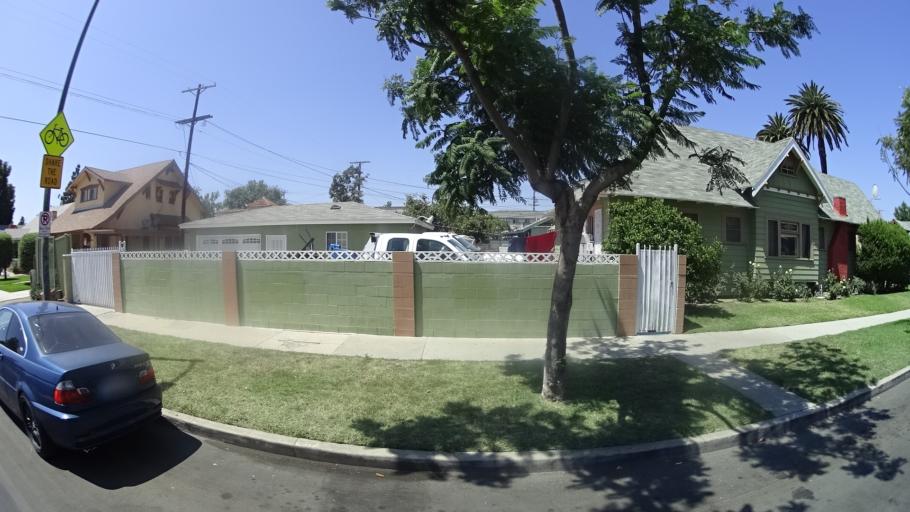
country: US
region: California
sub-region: Los Angeles County
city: View Park-Windsor Hills
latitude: 34.0027
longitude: -118.2962
